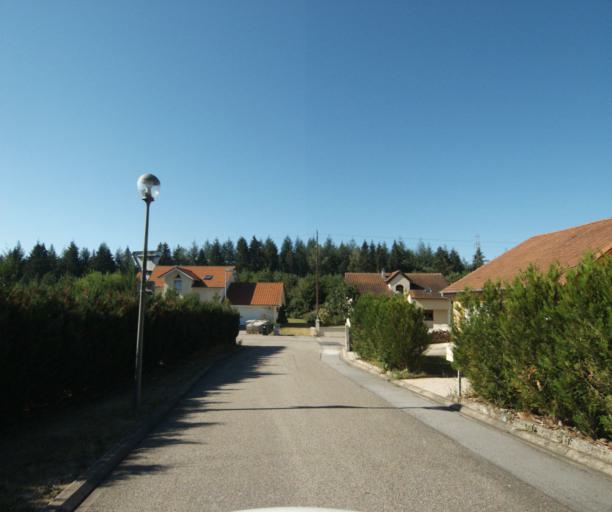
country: FR
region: Lorraine
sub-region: Departement des Vosges
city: Deyvillers
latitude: 48.1698
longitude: 6.5266
